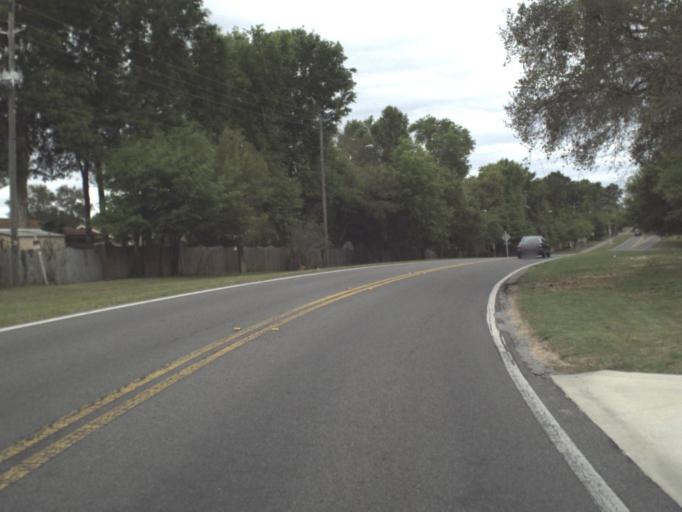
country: US
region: Florida
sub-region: Escambia County
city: East Pensacola Heights
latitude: 30.4441
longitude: -87.1818
